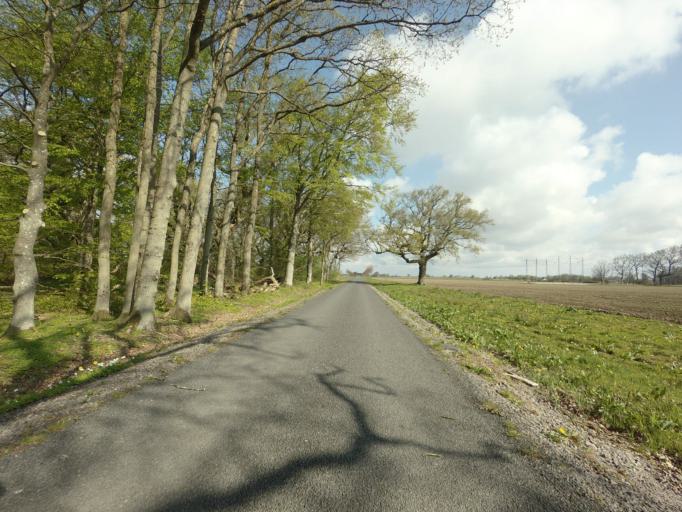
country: DK
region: Capital Region
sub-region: Helsingor Kommune
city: Hellebaek
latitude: 56.1338
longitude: 12.6140
